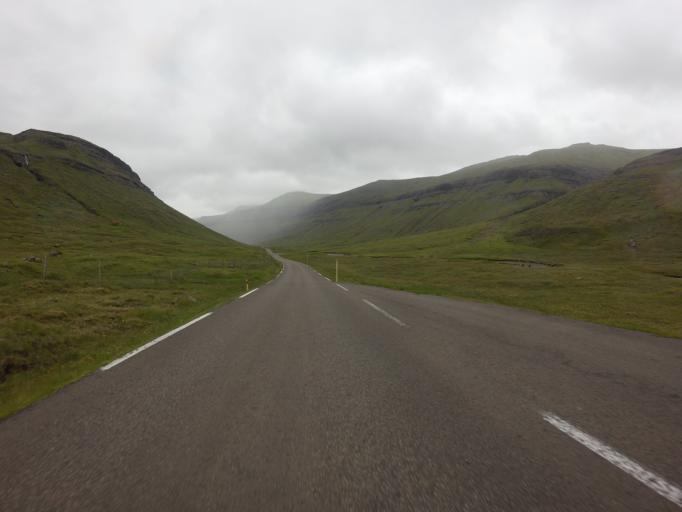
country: FO
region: Streymoy
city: Vestmanna
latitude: 62.2235
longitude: -7.1297
